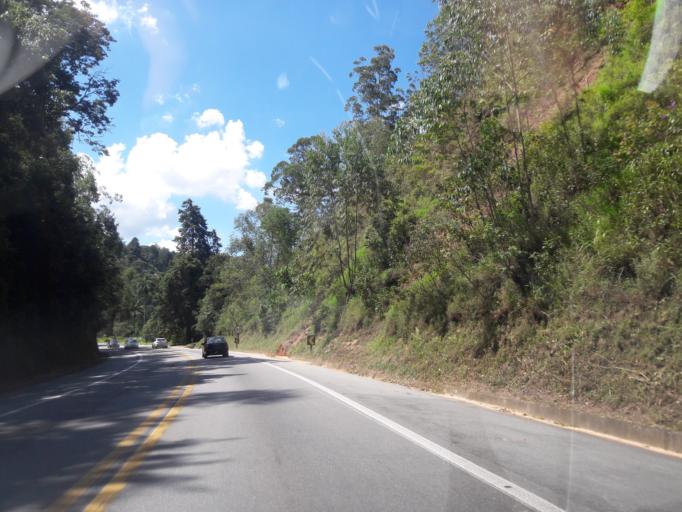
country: BR
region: Sao Paulo
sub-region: Francisco Morato
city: Francisco Morato
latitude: -23.2761
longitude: -46.7927
